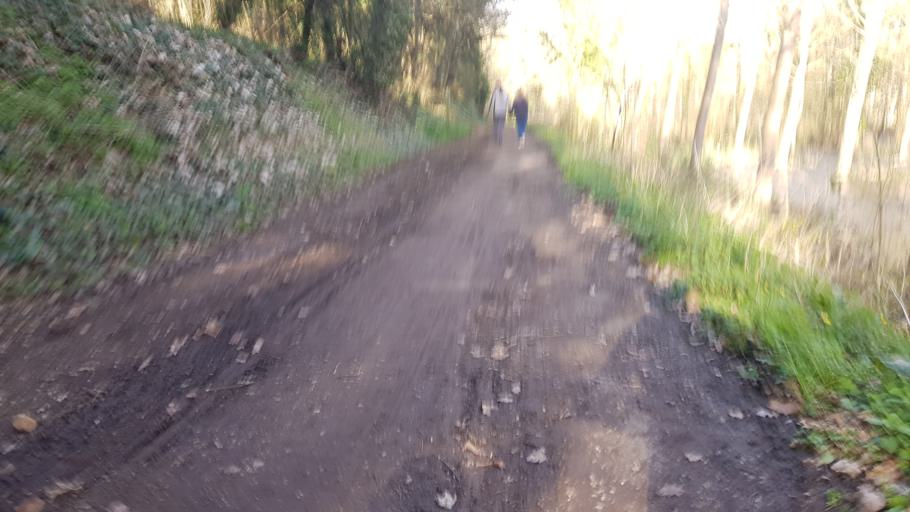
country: FR
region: Poitou-Charentes
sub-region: Departement de la Vienne
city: Migne-Auxances
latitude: 46.6288
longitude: 0.3221
